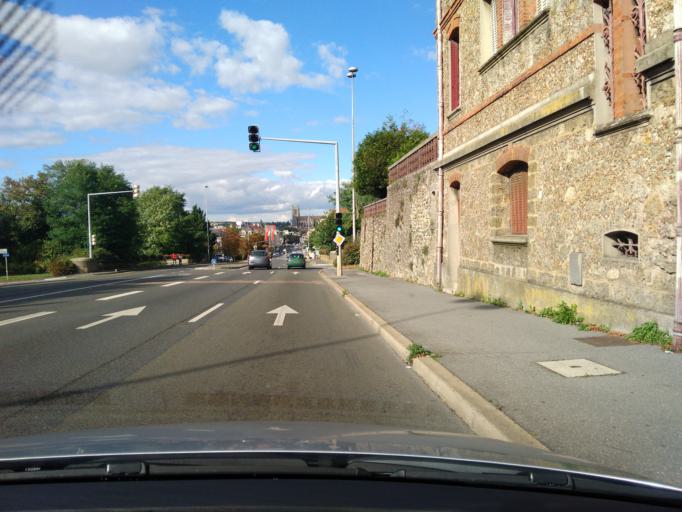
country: FR
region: Ile-de-France
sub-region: Departement de Seine-et-Marne
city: Meaux
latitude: 48.9501
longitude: 2.8800
